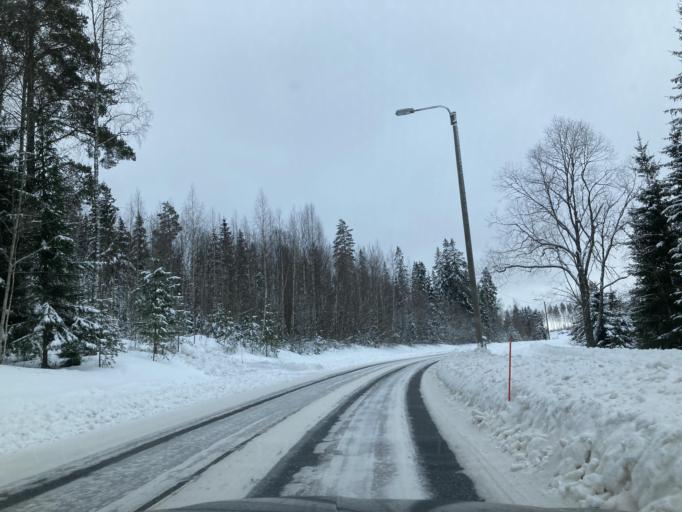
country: FI
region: Central Finland
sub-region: Jaemsae
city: Jaemsae
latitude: 61.8730
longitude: 25.2691
